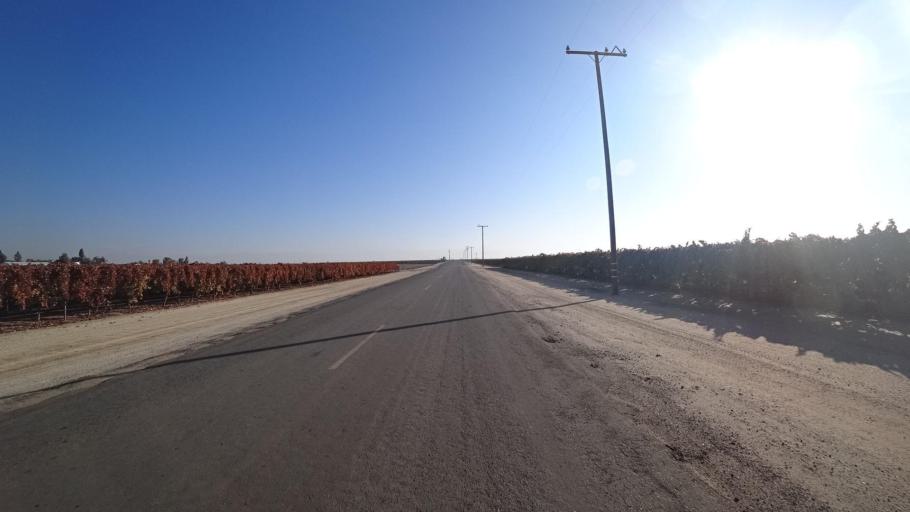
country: US
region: California
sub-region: Kern County
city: Delano
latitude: 35.7687
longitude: -119.1819
